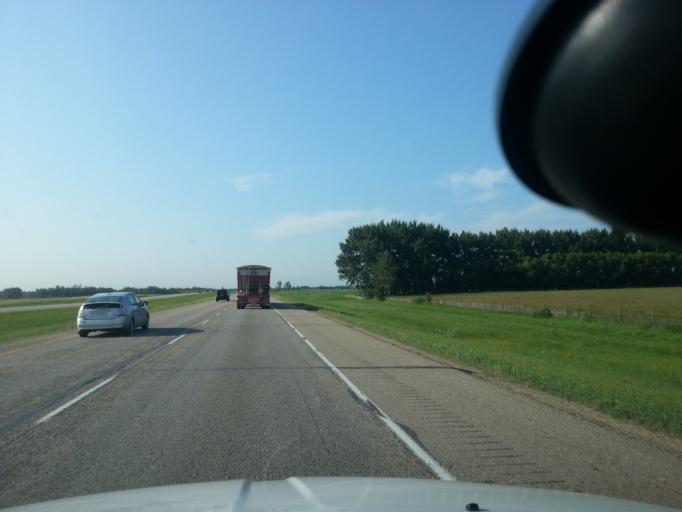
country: CA
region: Alberta
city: Millet
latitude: 52.9249
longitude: -113.6442
